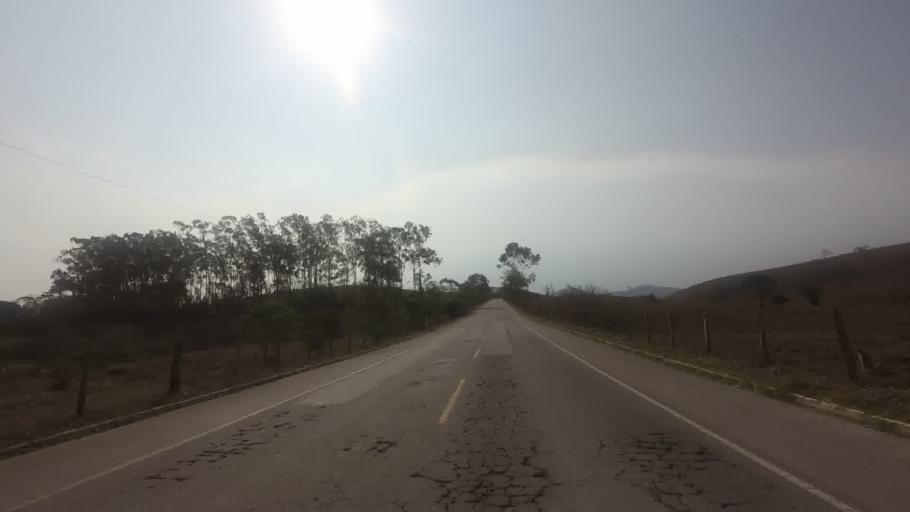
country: BR
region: Rio de Janeiro
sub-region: Bom Jesus Do Itabapoana
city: Bom Jesus do Itabapoana
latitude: -21.1426
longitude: -41.6282
